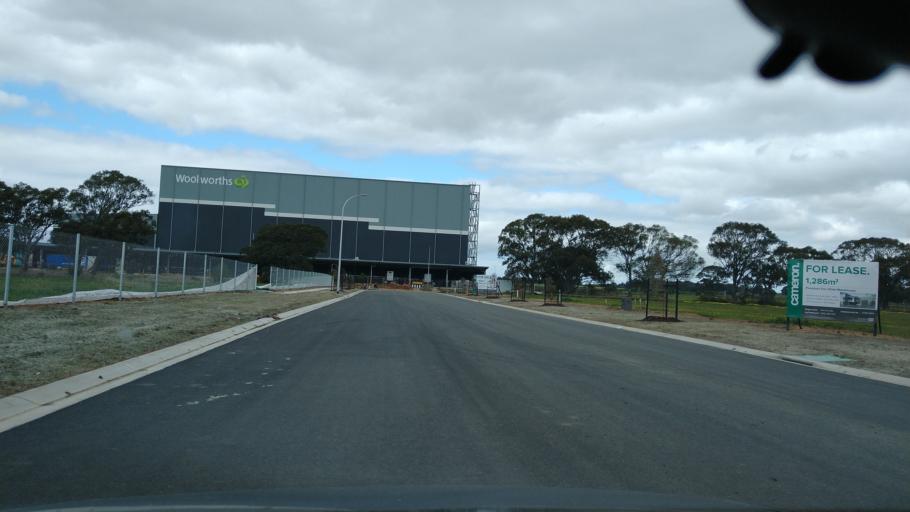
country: AU
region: Victoria
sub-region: Frankston
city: Sandhurst
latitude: -38.0556
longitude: 145.2234
